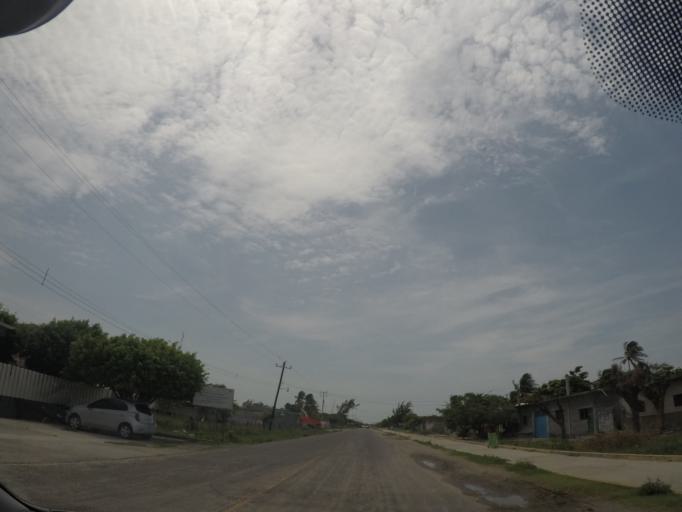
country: MX
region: Oaxaca
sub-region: San Mateo del Mar
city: Colonia Juarez
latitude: 16.2091
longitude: -95.0287
